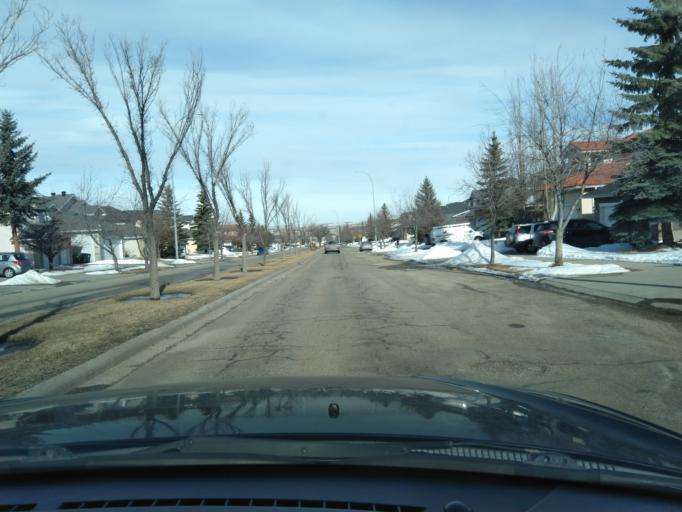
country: CA
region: Alberta
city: Calgary
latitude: 51.1370
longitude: -114.1308
